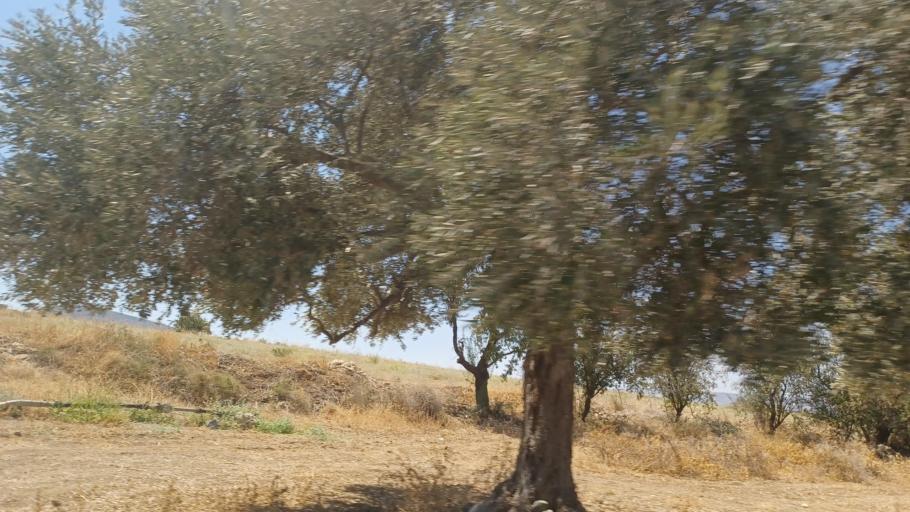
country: CY
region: Pafos
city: Polis
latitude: 35.0540
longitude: 32.4673
